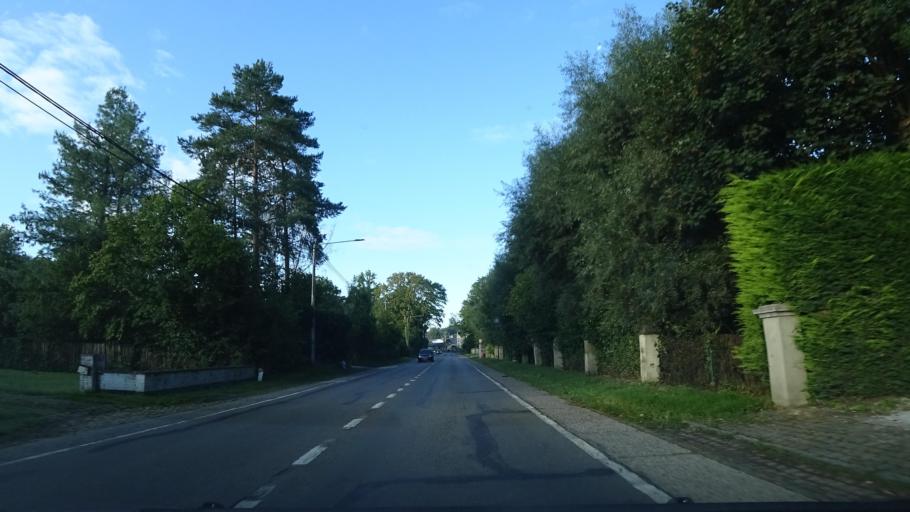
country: BE
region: Wallonia
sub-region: Province du Brabant Wallon
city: Court-Saint-Etienne
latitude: 50.6346
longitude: 4.5386
